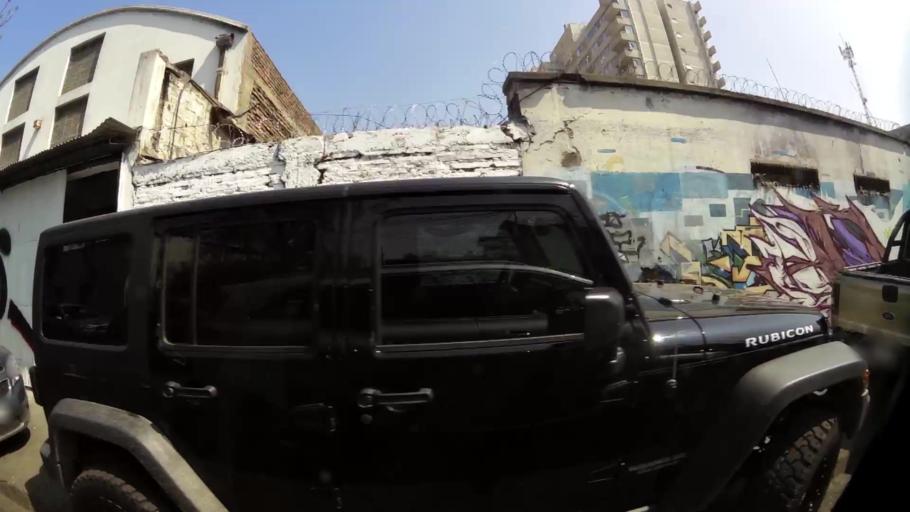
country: CL
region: Santiago Metropolitan
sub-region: Provincia de Santiago
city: Santiago
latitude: -33.4567
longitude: -70.6548
